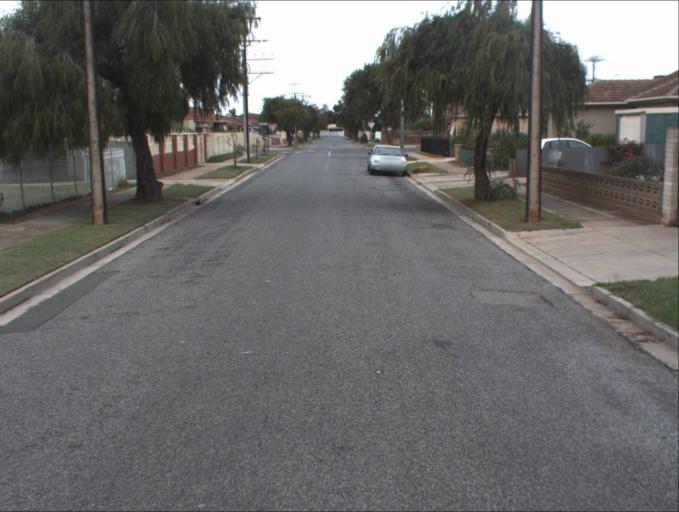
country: AU
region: South Australia
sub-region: Charles Sturt
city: Woodville North
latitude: -34.8694
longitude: 138.5586
